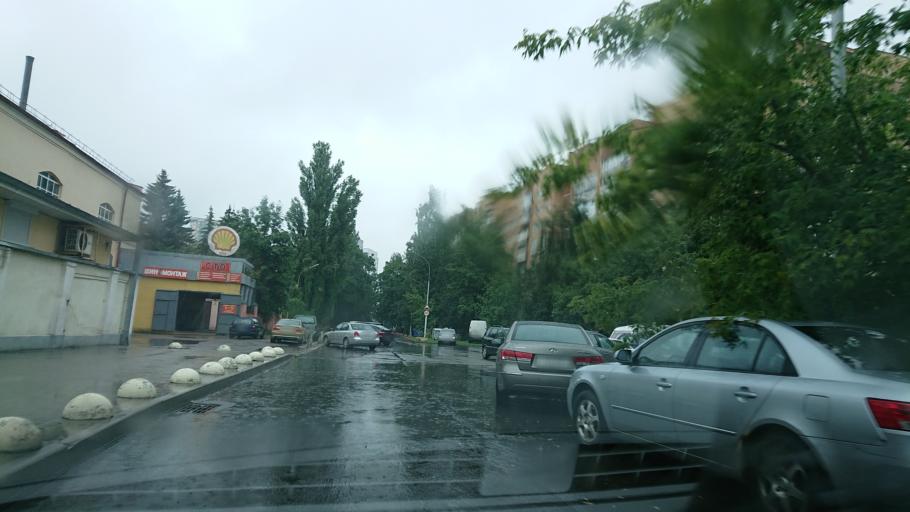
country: BY
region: Minsk
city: Minsk
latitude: 53.9230
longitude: 27.5641
